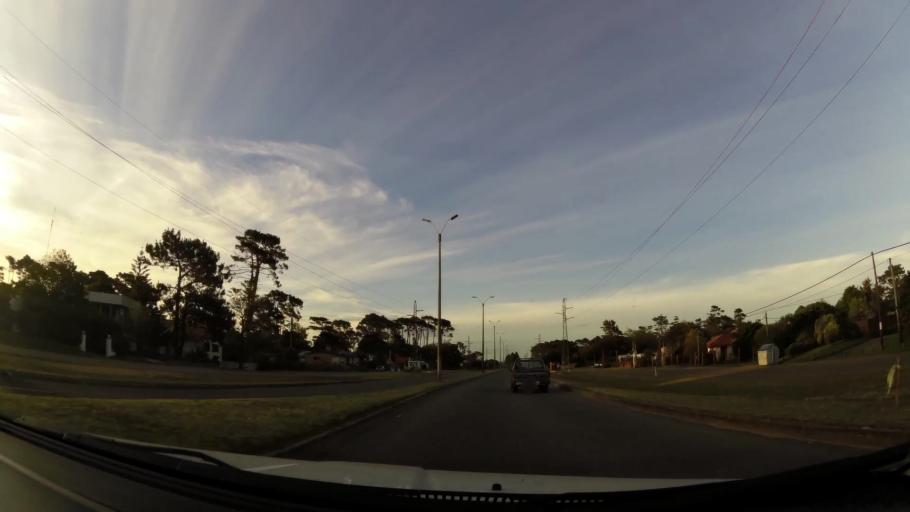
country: UY
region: Maldonado
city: Maldonado
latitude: -34.9245
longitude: -54.9416
